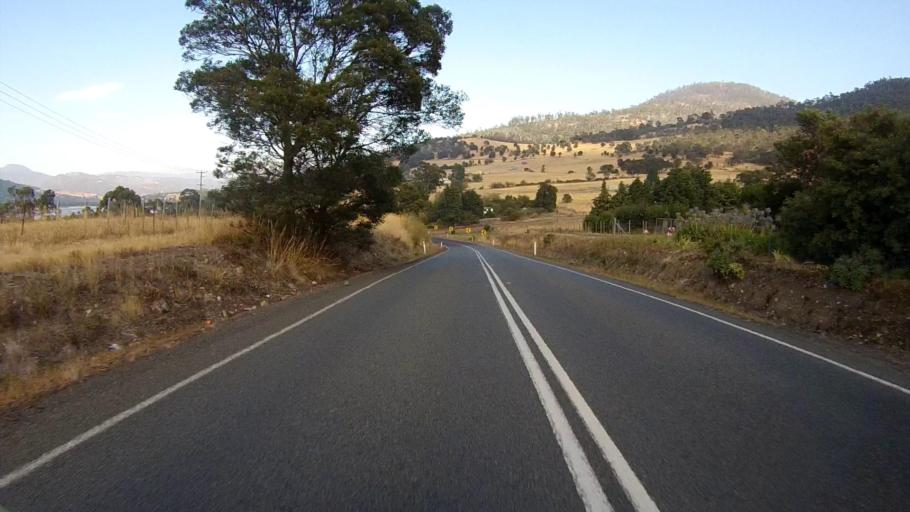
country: AU
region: Tasmania
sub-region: Glenorchy
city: Granton
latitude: -42.7488
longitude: 147.1549
